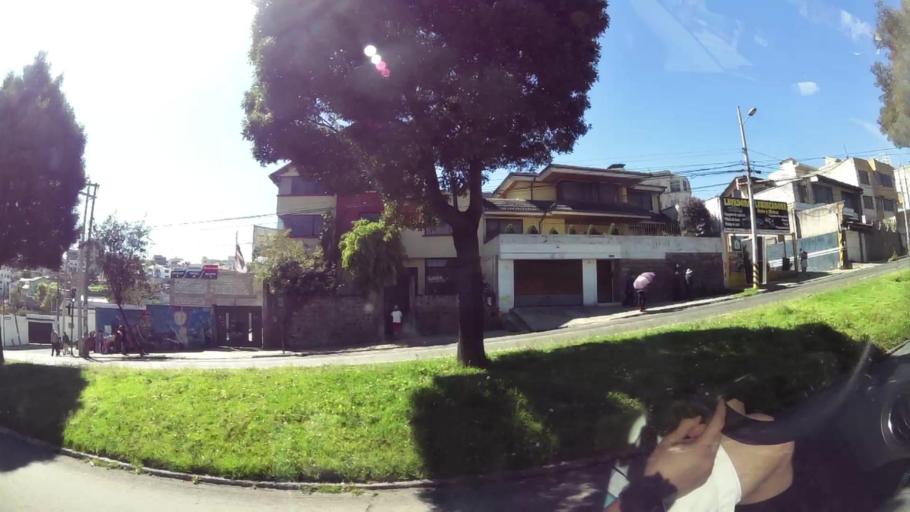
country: EC
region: Pichincha
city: Quito
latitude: -0.1557
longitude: -78.4661
